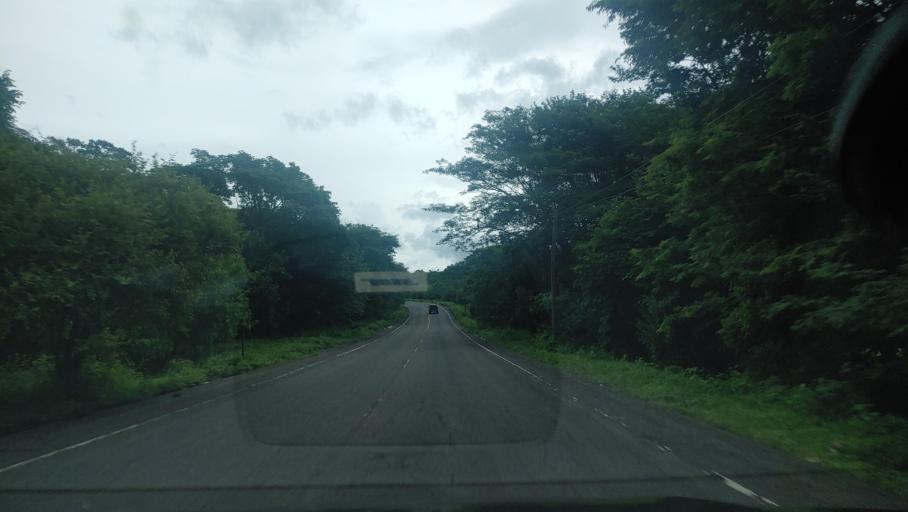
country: HN
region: Choluteca
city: Santa Ana de Yusguare
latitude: 13.3677
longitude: -87.0786
